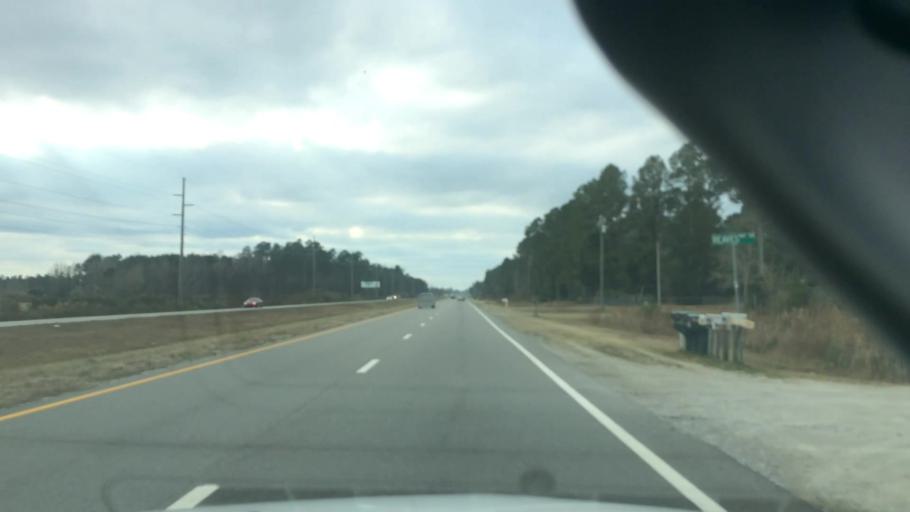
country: US
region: North Carolina
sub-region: Brunswick County
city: Sunset Beach
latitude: 33.9427
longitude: -78.5283
